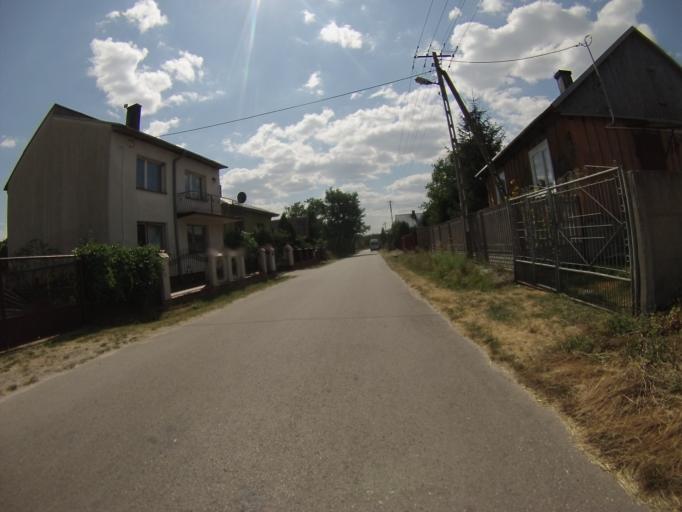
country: PL
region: Swietokrzyskie
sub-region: Powiat kielecki
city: Rakow
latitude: 50.6979
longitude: 21.0903
